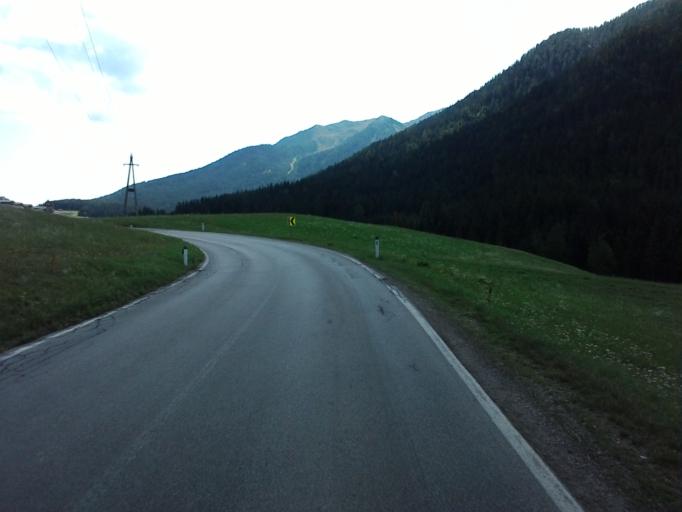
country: AT
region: Tyrol
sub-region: Politischer Bezirk Lienz
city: Kartitsch
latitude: 46.7234
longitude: 12.5034
